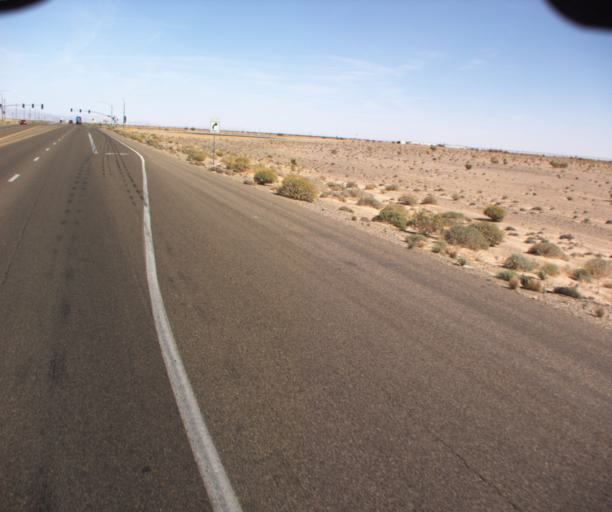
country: MX
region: Sonora
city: San Luis Rio Colorado
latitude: 32.4947
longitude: -114.7033
